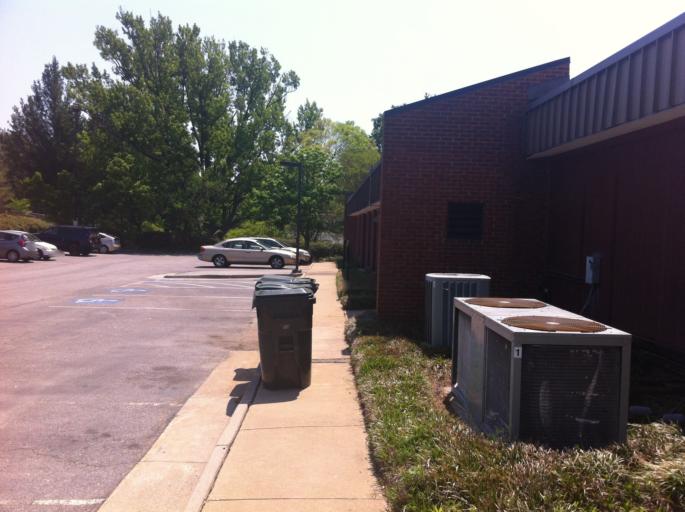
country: US
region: Virginia
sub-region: Henrico County
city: Dumbarton
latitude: 37.5777
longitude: -77.5115
